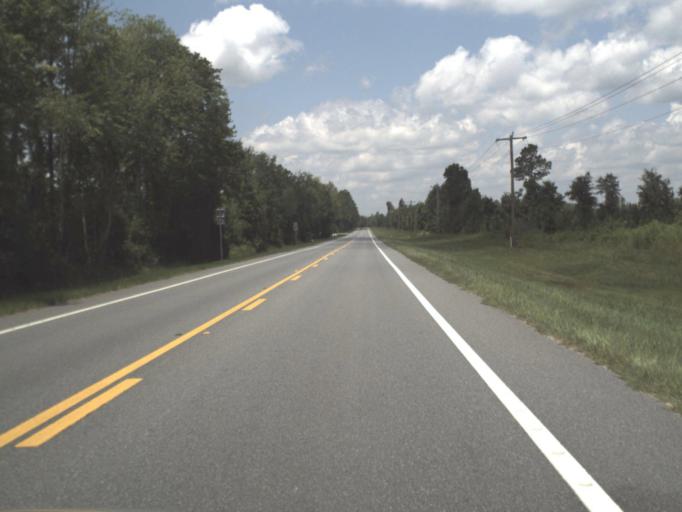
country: US
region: Florida
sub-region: Union County
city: Lake Butler
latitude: 30.0080
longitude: -82.4678
